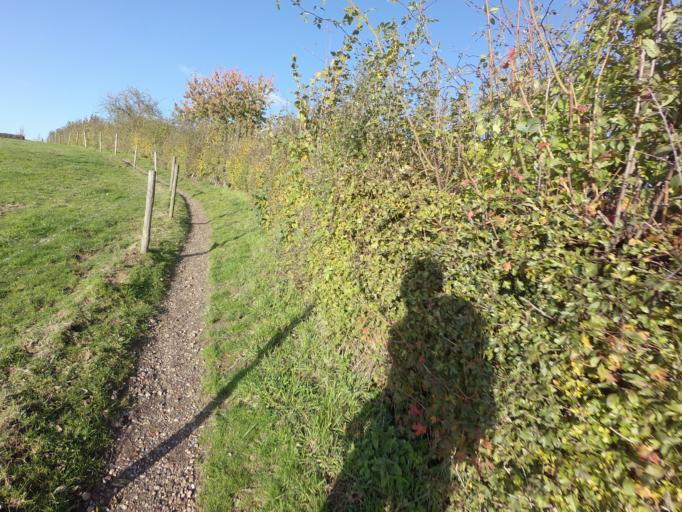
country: BE
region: Wallonia
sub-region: Province de Liege
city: Plombieres
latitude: 50.7655
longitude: 5.9346
